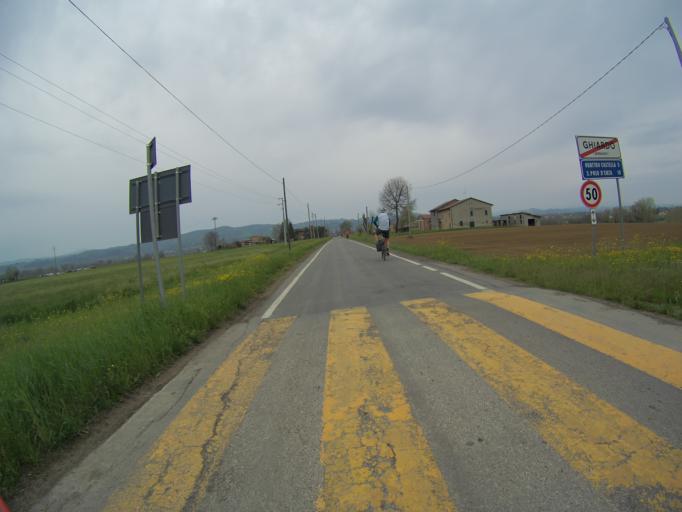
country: IT
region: Emilia-Romagna
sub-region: Provincia di Reggio Emilia
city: Bibbiano
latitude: 44.6613
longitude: 10.4977
